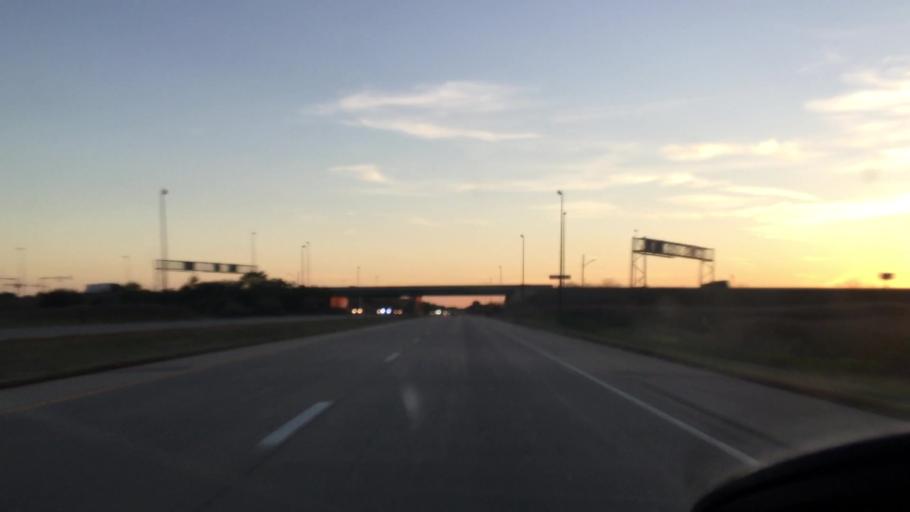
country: US
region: Illinois
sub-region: Grundy County
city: Morris
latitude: 41.3900
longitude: -88.4202
